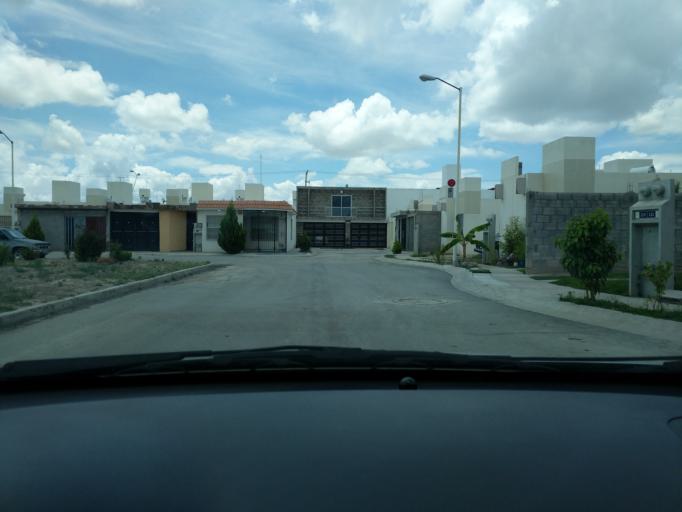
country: MX
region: San Luis Potosi
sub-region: San Luis Potosi
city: Fraccion Milpillas
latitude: 22.2216
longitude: -100.9346
